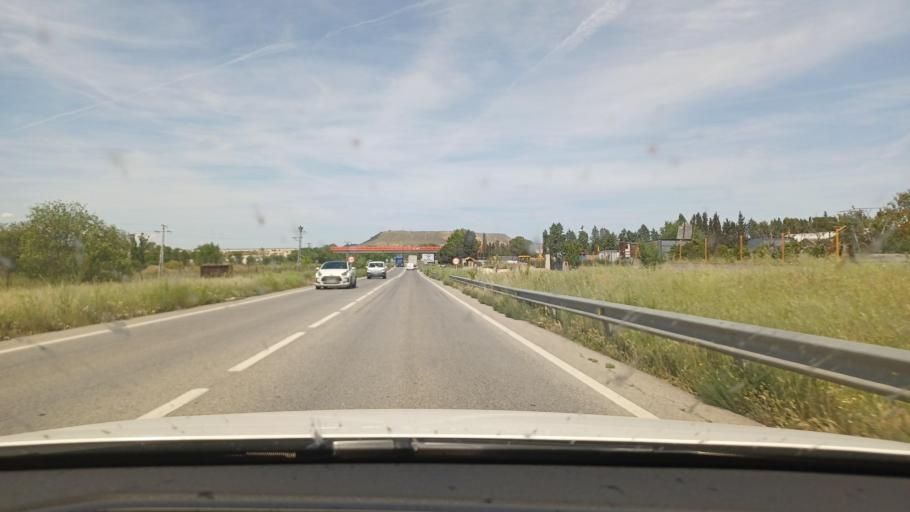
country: ES
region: Madrid
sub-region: Provincia de Madrid
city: Torrejon de Ardoz
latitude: 40.4282
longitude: -3.4486
